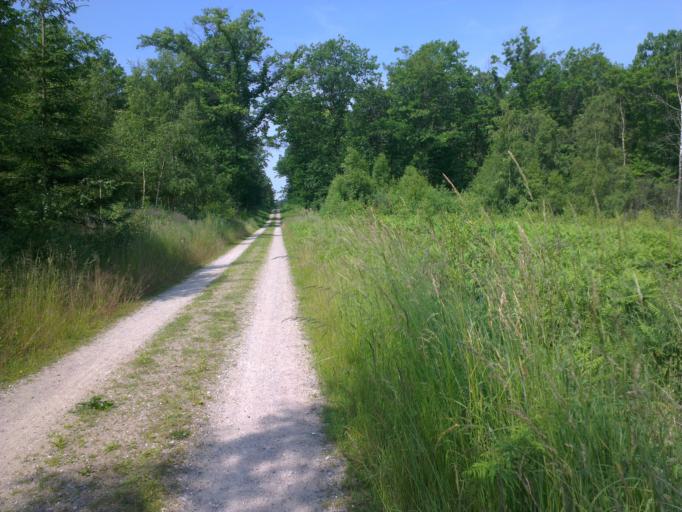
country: DK
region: Capital Region
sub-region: Allerod Kommune
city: Lillerod
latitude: 55.9122
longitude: 12.3637
